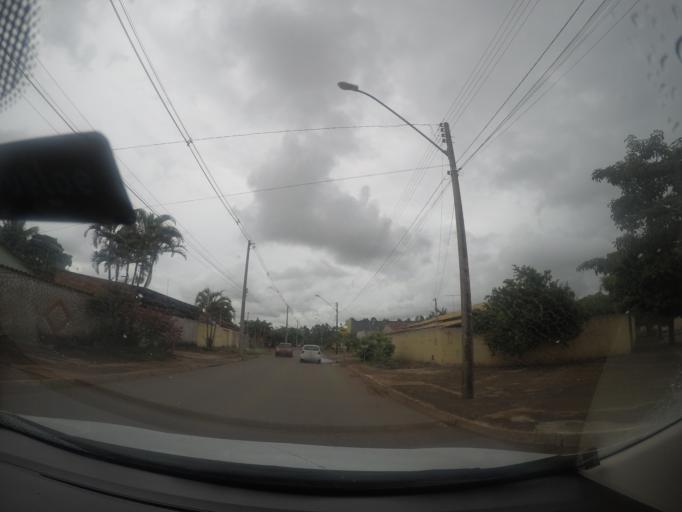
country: BR
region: Goias
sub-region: Trindade
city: Trindade
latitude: -16.6496
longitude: -49.3860
